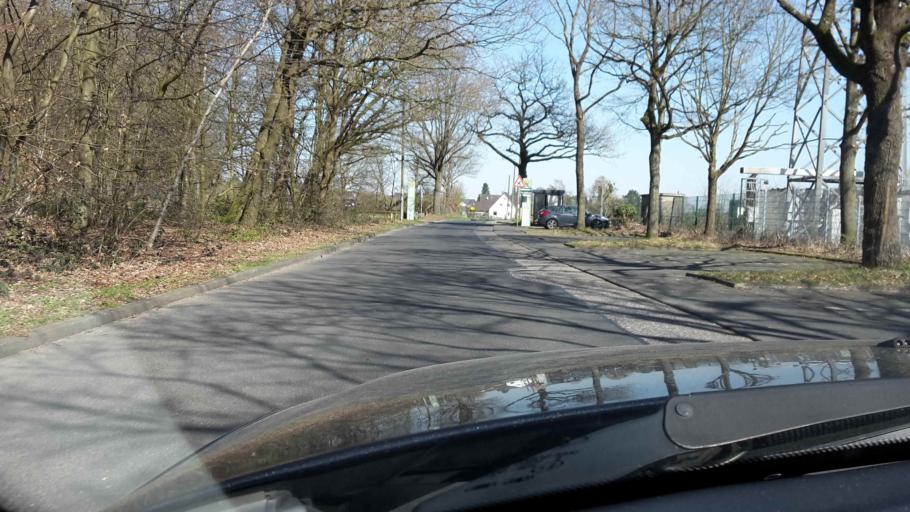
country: DE
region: North Rhine-Westphalia
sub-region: Regierungsbezirk Koln
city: Wachtberg
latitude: 50.6371
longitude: 7.0823
